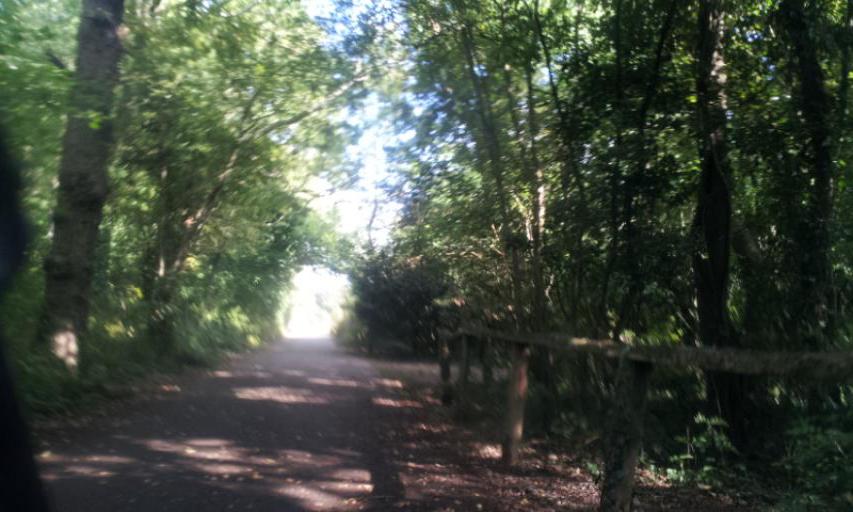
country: GB
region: England
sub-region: Greater London
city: Chislehurst
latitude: 51.3937
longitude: 0.0640
